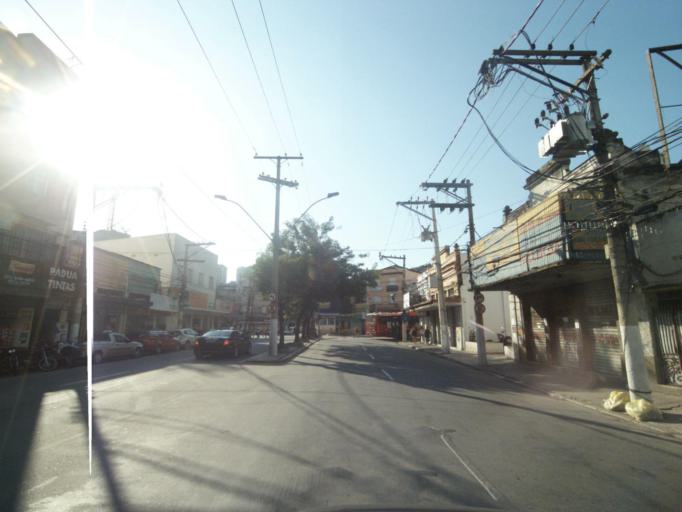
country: BR
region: Rio de Janeiro
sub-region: Niteroi
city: Niteroi
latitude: -22.8987
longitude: -43.1032
